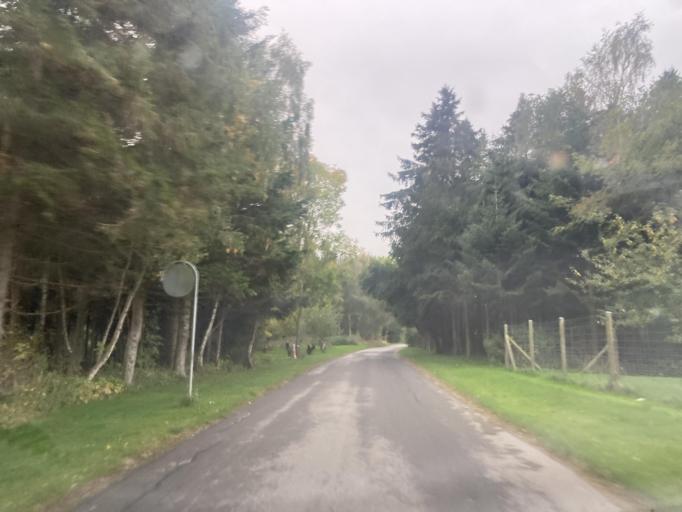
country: DK
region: Capital Region
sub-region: Egedal Kommune
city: Vekso
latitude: 55.7230
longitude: 12.2162
